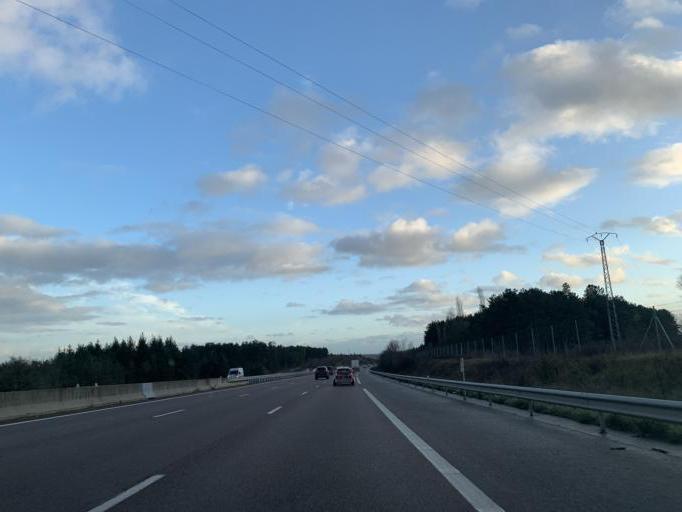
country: FR
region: Bourgogne
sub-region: Departement de la Cote-d'Or
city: Selongey
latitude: 47.6036
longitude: 5.1988
